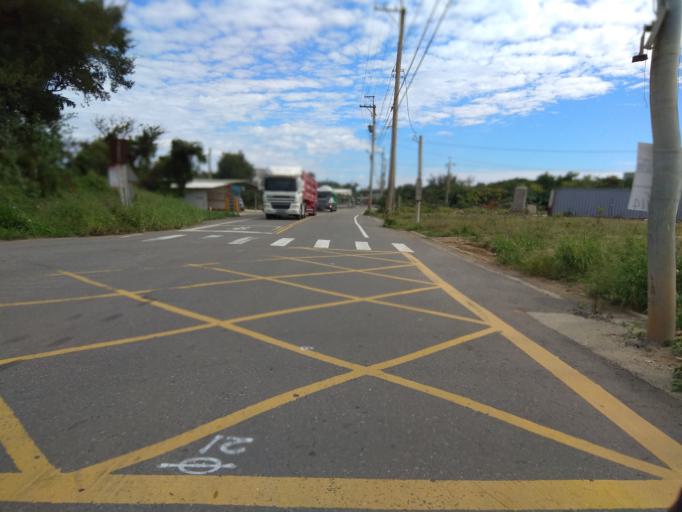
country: TW
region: Taiwan
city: Taoyuan City
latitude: 25.0625
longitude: 121.1297
